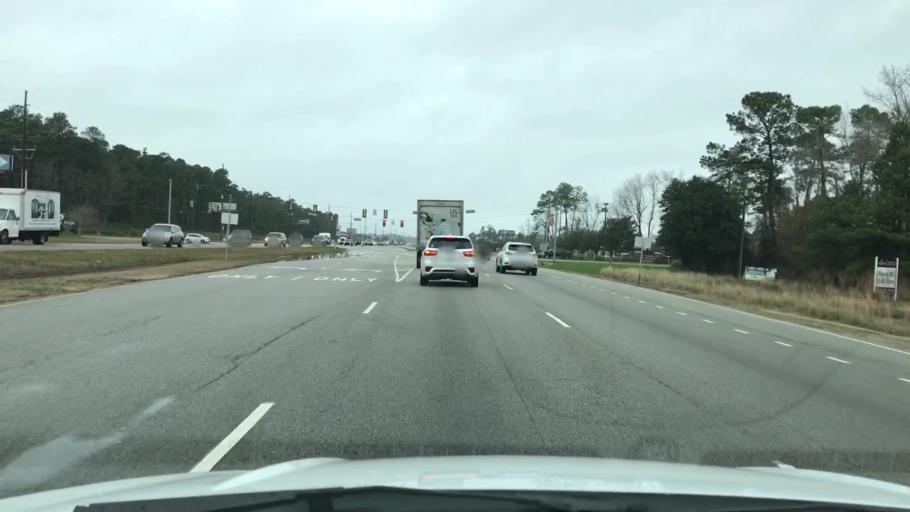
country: US
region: South Carolina
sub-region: Horry County
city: Red Hill
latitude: 33.7814
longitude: -78.9884
